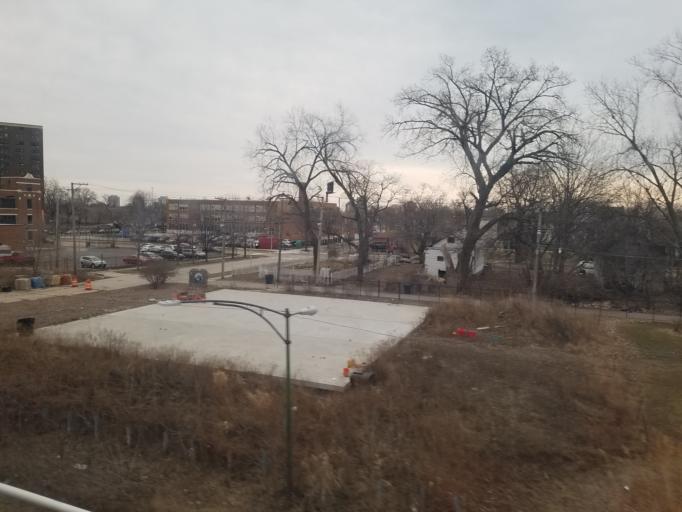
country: US
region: Illinois
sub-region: Cook County
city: Chicago
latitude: 41.8148
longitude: -87.6357
